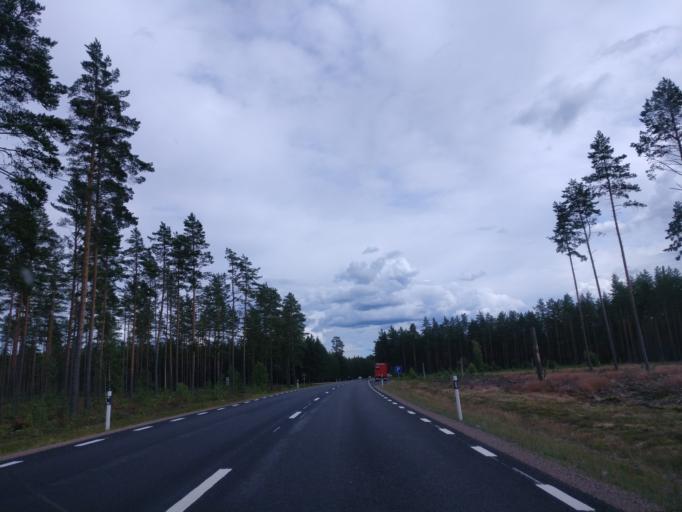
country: SE
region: Vaermland
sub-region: Hagfors Kommun
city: Hagfors
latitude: 60.0452
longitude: 13.5789
